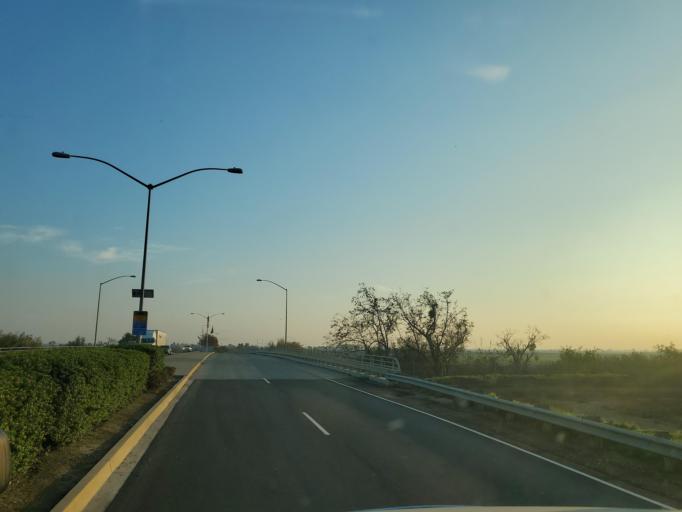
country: US
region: California
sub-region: San Joaquin County
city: Country Club
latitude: 37.9415
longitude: -121.3589
